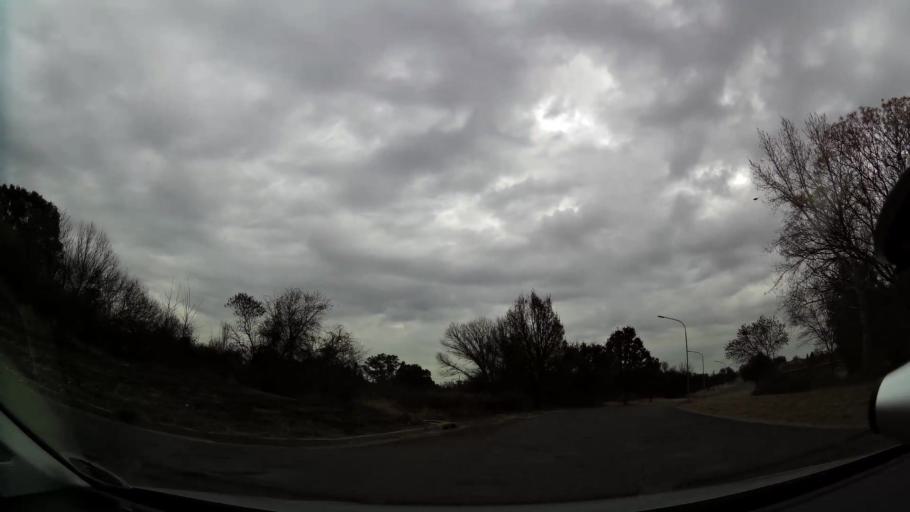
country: ZA
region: Orange Free State
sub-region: Fezile Dabi District Municipality
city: Kroonstad
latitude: -27.6516
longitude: 27.2439
